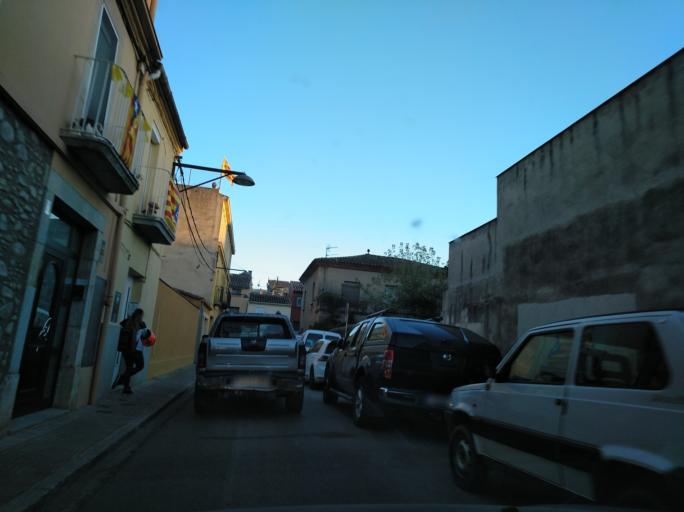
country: ES
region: Catalonia
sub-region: Provincia de Girona
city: Salt
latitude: 41.9736
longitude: 2.7834
